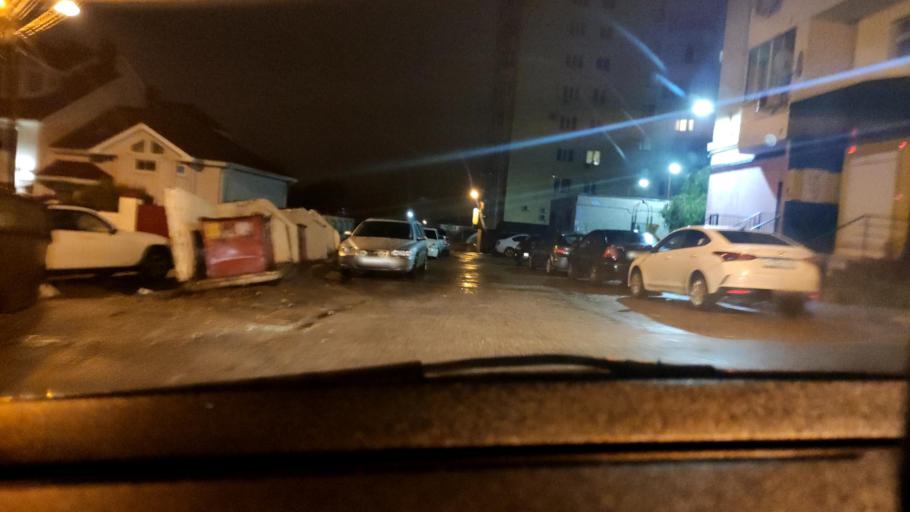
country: RU
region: Voronezj
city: Voronezh
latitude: 51.6420
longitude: 39.2049
